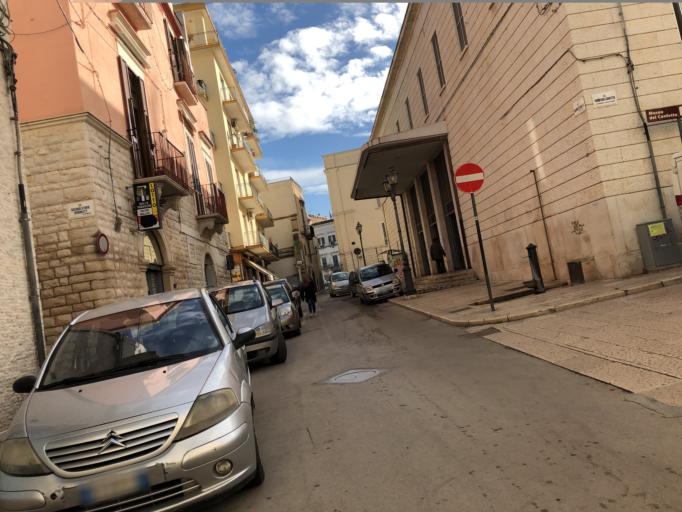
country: IT
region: Apulia
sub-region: Provincia di Barletta - Andria - Trani
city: Andria
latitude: 41.2265
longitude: 16.2953
